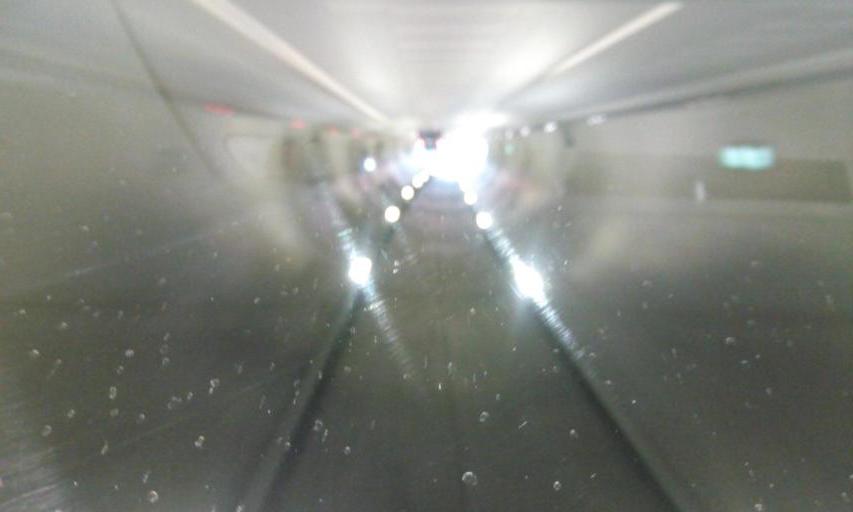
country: TR
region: Istanbul
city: UEskuedar
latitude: 41.0220
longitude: 29.0639
